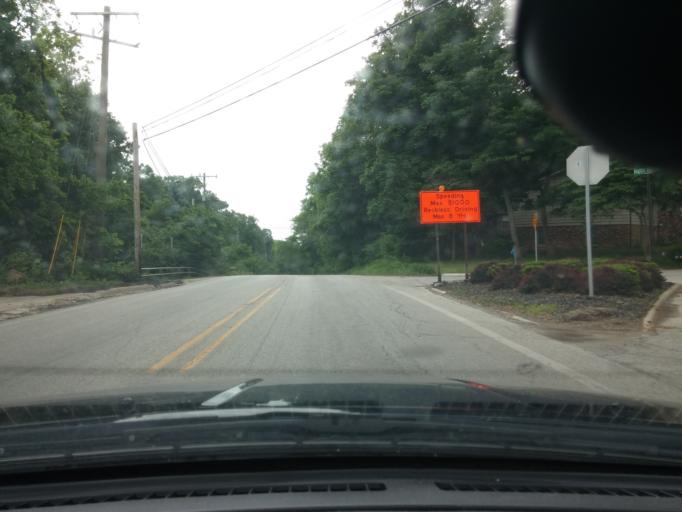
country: US
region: Indiana
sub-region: Tippecanoe County
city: West Lafayette
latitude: 40.4436
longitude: -86.8996
